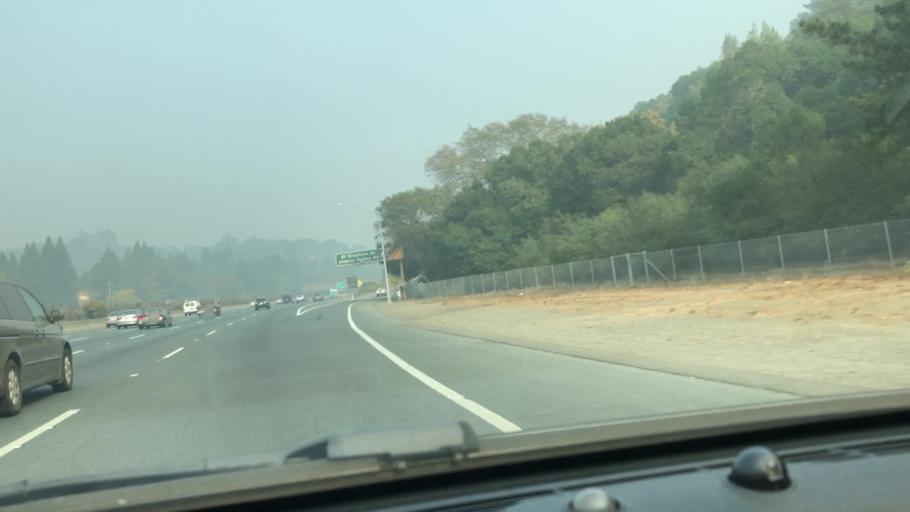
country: US
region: California
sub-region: Contra Costa County
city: Orinda
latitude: 37.8888
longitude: -122.1754
